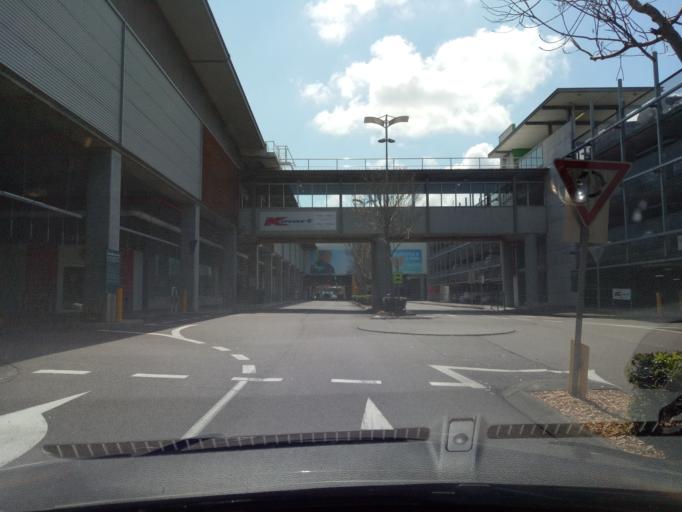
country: AU
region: New South Wales
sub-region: Gosford Shire
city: Erina
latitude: -33.4385
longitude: 151.3919
